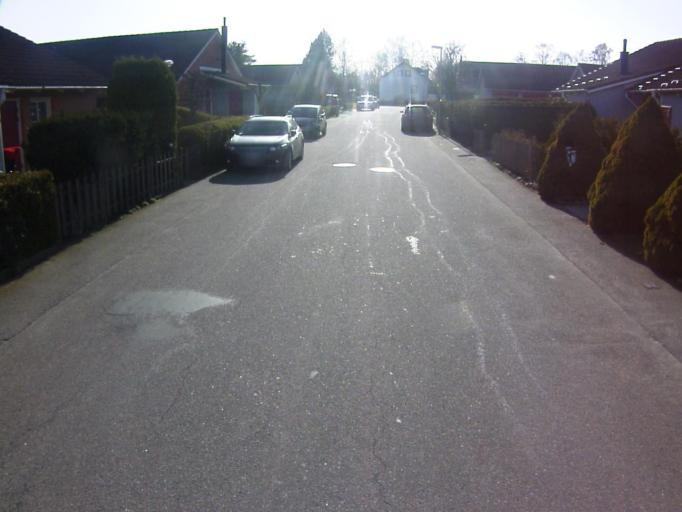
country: SE
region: Skane
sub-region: Kavlinge Kommun
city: Kaevlinge
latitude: 55.8033
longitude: 13.1095
